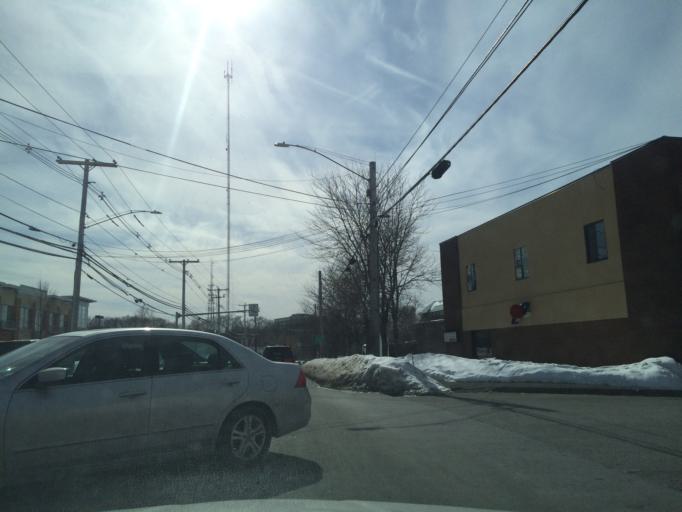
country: US
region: Massachusetts
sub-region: Middlesex County
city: Newton
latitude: 42.3088
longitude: -71.2152
